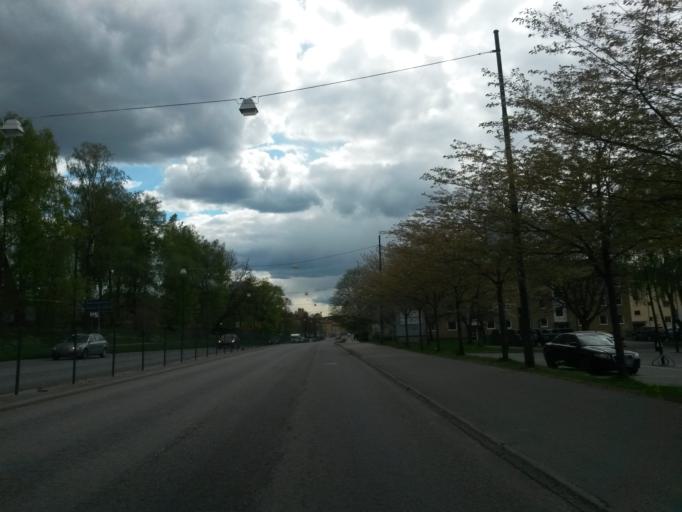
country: SE
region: Vaestra Goetaland
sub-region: Boras Kommun
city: Boras
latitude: 57.7488
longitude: 12.9448
